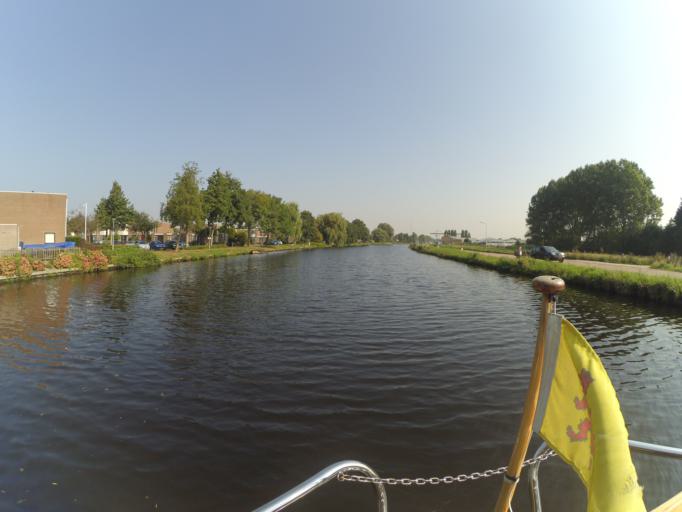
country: NL
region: North Holland
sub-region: Gemeente Heemstede
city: Heemstede
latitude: 52.3322
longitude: 4.6178
